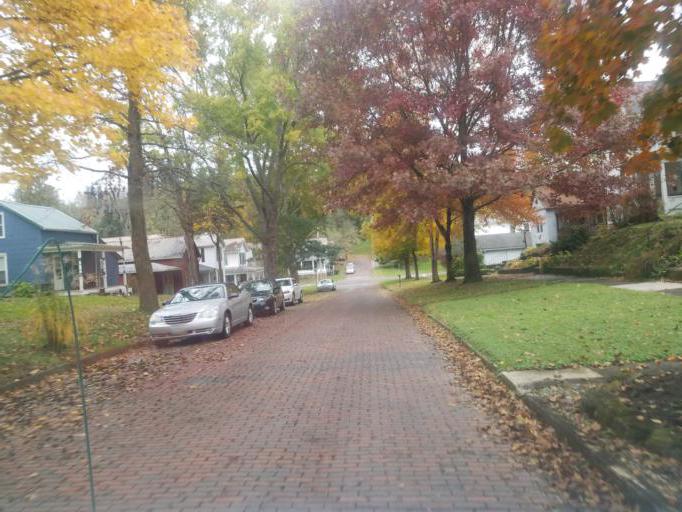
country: US
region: Ohio
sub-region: Washington County
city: Marietta
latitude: 39.4285
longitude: -81.4576
